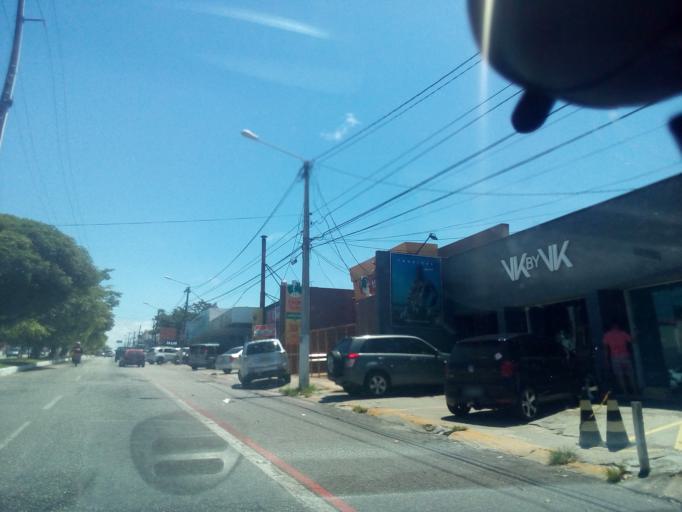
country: BR
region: Rio Grande do Norte
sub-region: Natal
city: Natal
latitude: -5.8334
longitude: -35.2182
